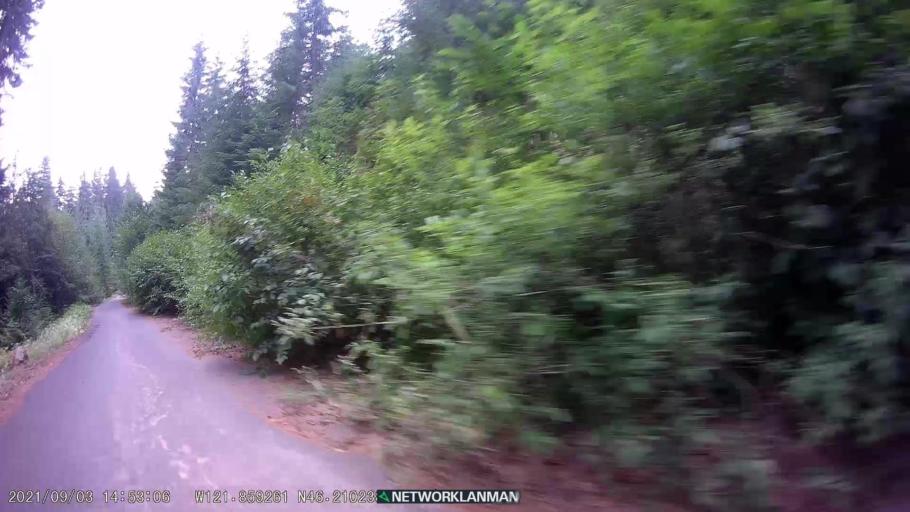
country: US
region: Washington
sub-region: Skamania County
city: Carson
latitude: 46.2101
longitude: -121.8590
